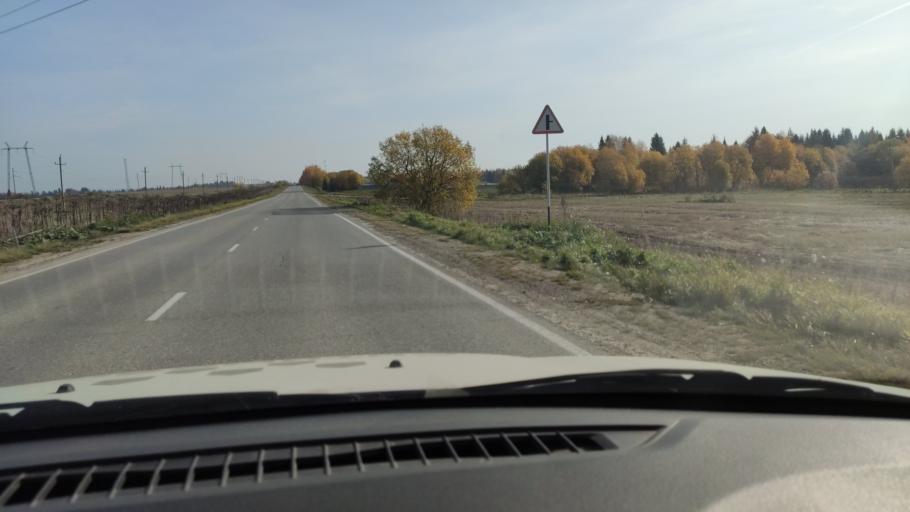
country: RU
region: Perm
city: Sylva
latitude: 58.0297
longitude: 56.6965
